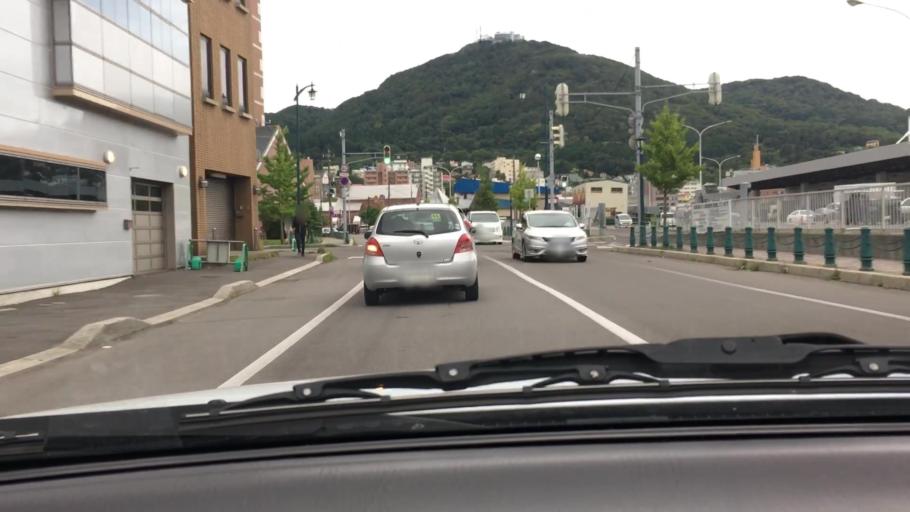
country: JP
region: Hokkaido
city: Hakodate
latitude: 41.7687
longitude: 140.7194
